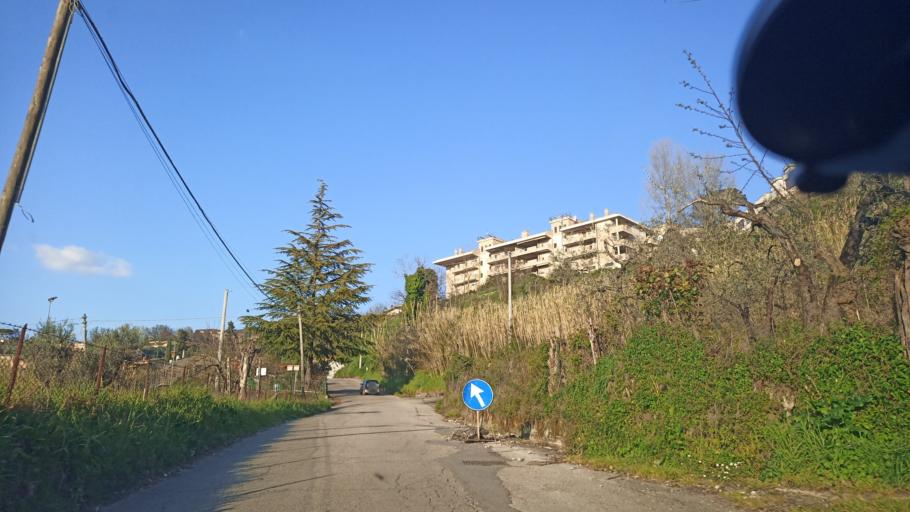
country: IT
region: Latium
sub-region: Provincia di Rieti
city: Poggio Mirteto
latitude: 42.2659
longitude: 12.6829
